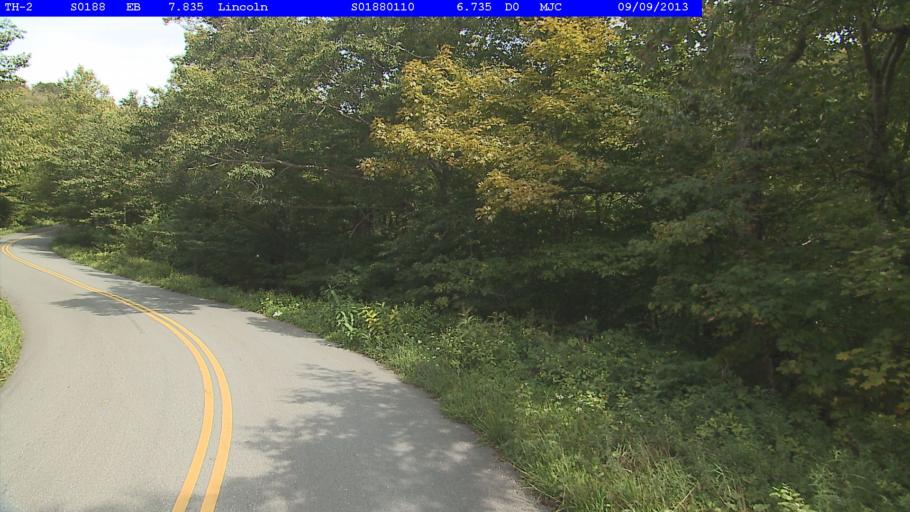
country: US
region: Vermont
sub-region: Addison County
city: Bristol
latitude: 44.0947
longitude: -72.9320
